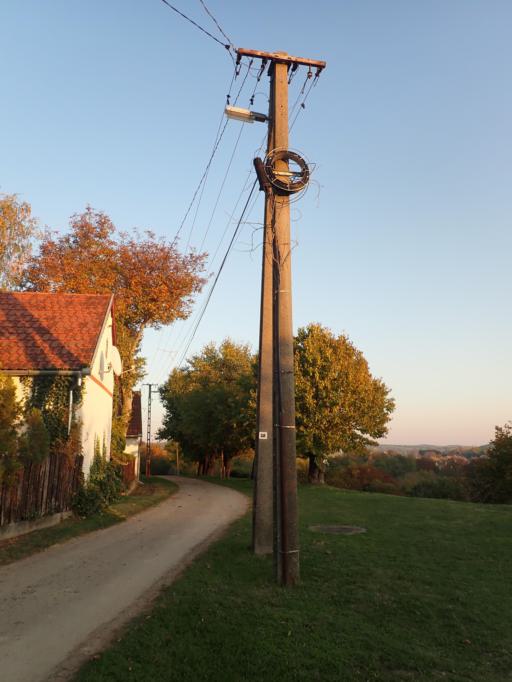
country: HU
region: Baranya
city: Kozarmisleny
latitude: 46.0345
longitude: 18.3833
